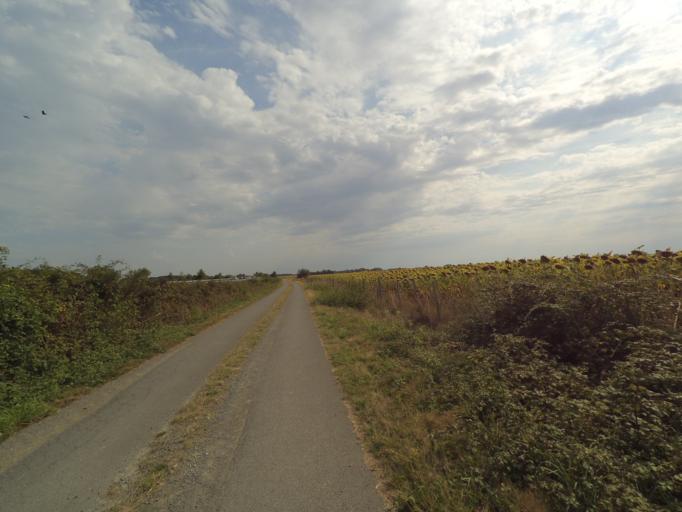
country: FR
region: Pays de la Loire
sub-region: Departement de la Vendee
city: Bouffere
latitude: 46.9907
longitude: -1.3820
